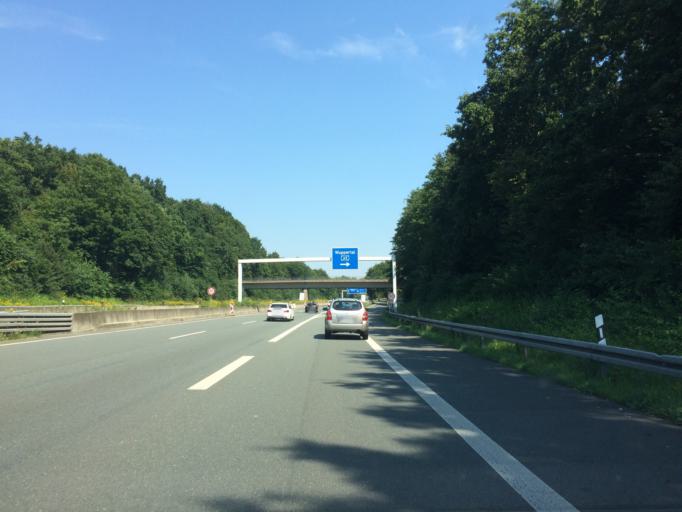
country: DE
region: North Rhine-Westphalia
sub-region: Regierungsbezirk Munster
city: Haltern
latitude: 51.7013
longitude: 7.1427
